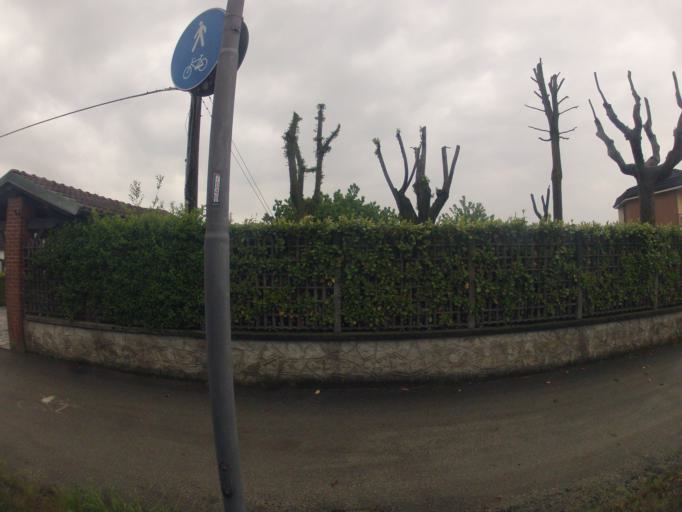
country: IT
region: Piedmont
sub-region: Provincia di Cuneo
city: Polonghera
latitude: 44.8053
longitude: 7.6048
